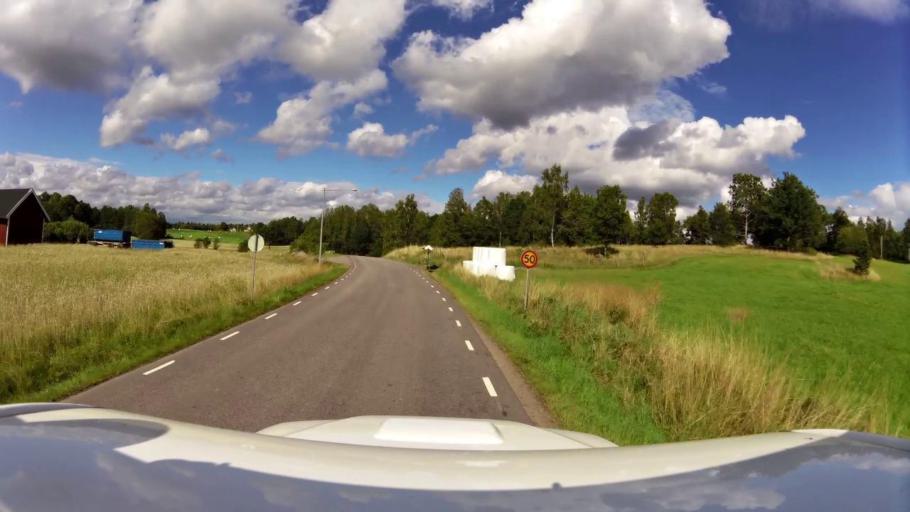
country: SE
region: OEstergoetland
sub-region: Kinda Kommun
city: Rimforsa
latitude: 58.2238
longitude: 15.6841
